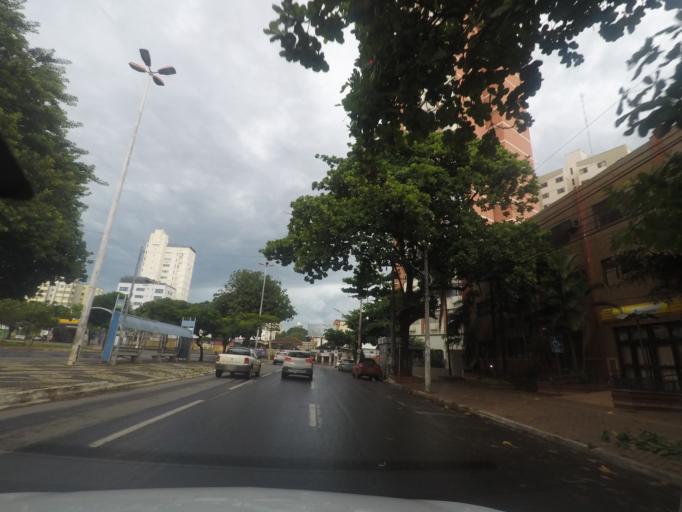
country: BR
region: Goias
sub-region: Goiania
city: Goiania
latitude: -16.6800
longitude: -49.2576
